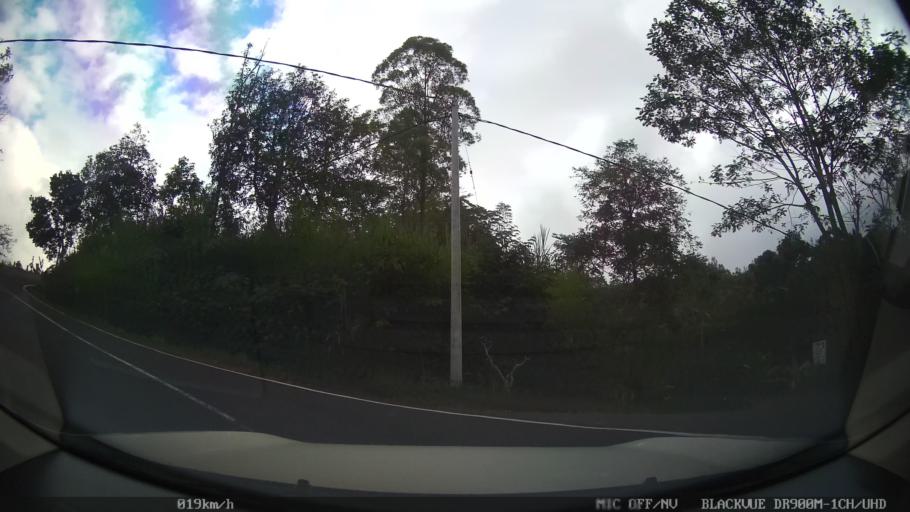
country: ID
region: Bali
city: Banjar Kedisan
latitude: -8.2584
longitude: 115.3442
